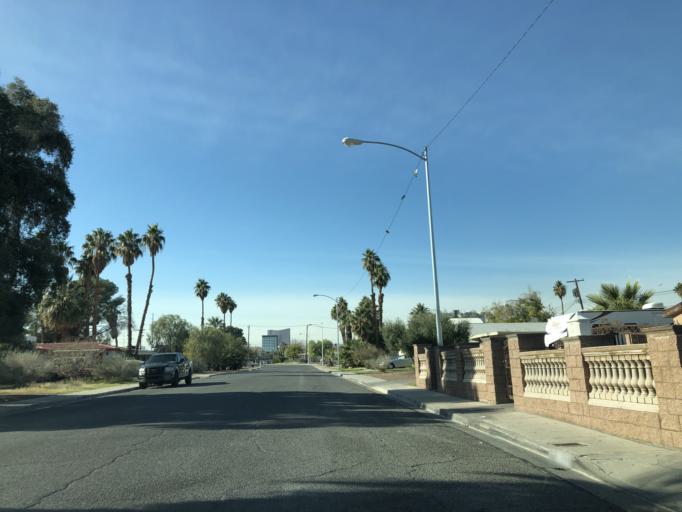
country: US
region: Nevada
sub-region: Clark County
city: Winchester
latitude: 36.1309
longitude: -115.1297
